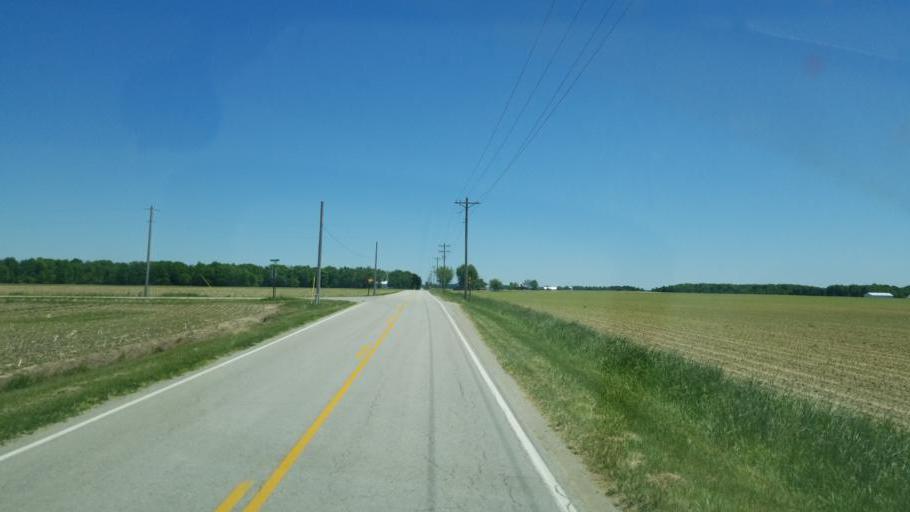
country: US
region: Ohio
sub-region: Darke County
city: Ansonia
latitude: 40.2649
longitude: -84.6952
